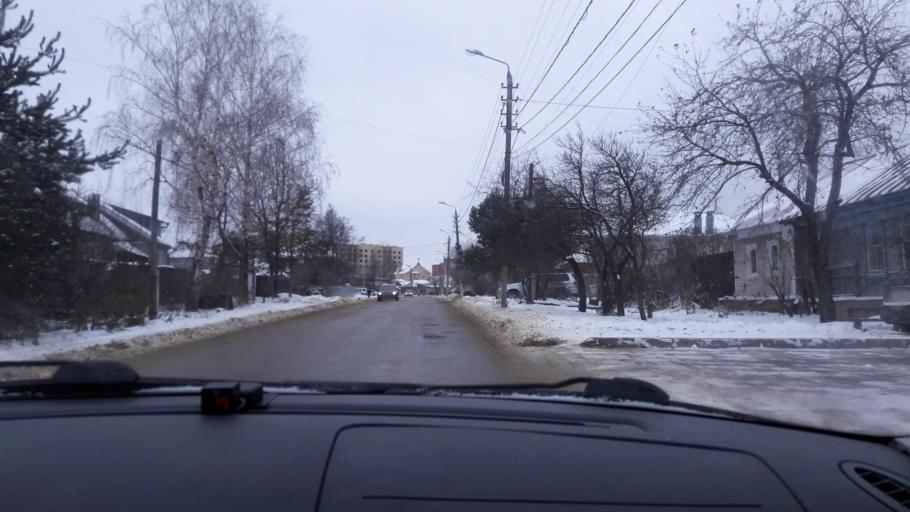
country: RU
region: Tula
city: Gorelki
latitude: 54.2344
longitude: 37.6321
